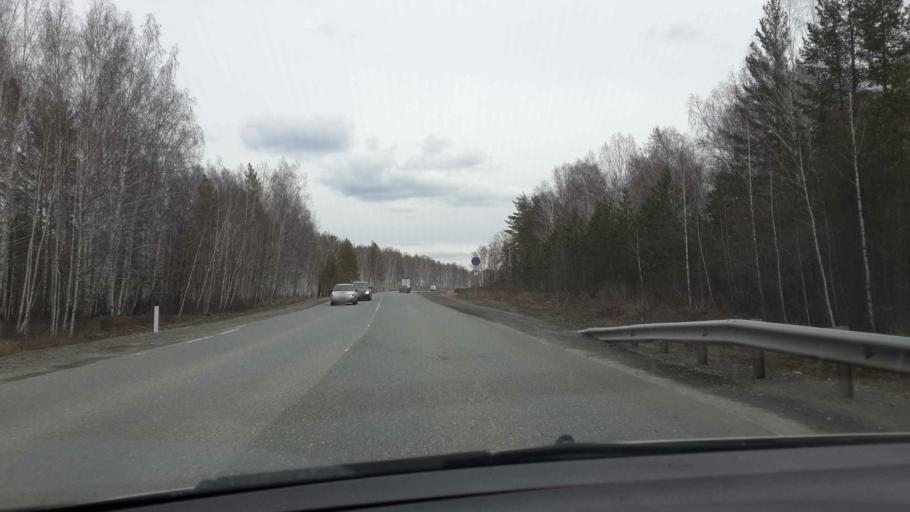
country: RU
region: Sverdlovsk
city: Zarechnyy
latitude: 56.7409
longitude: 61.2241
